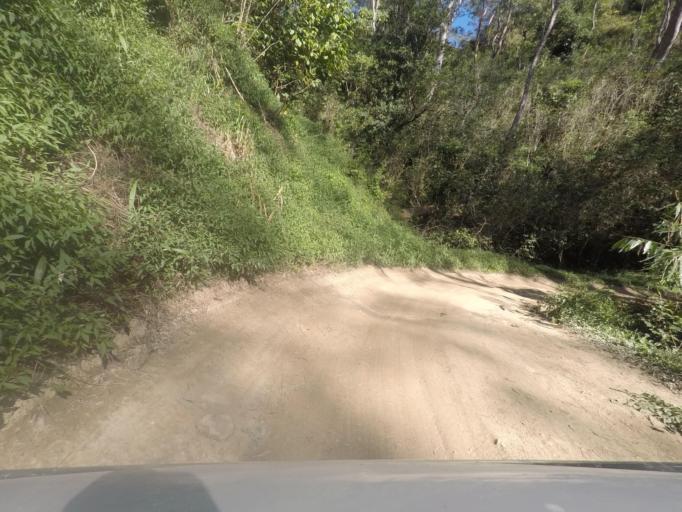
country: TL
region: Ermera
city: Gleno
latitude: -8.7405
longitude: 125.3464
